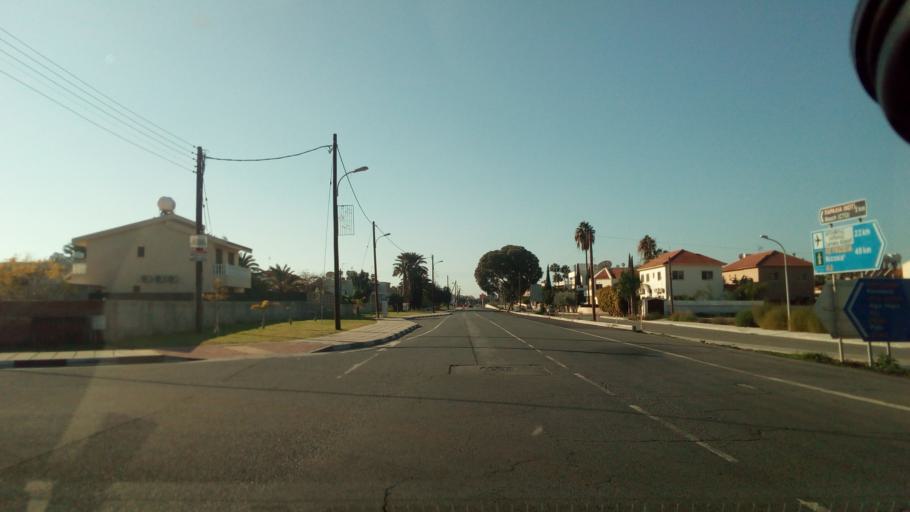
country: CY
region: Larnaka
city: Voroklini
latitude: 34.9780
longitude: 33.6752
